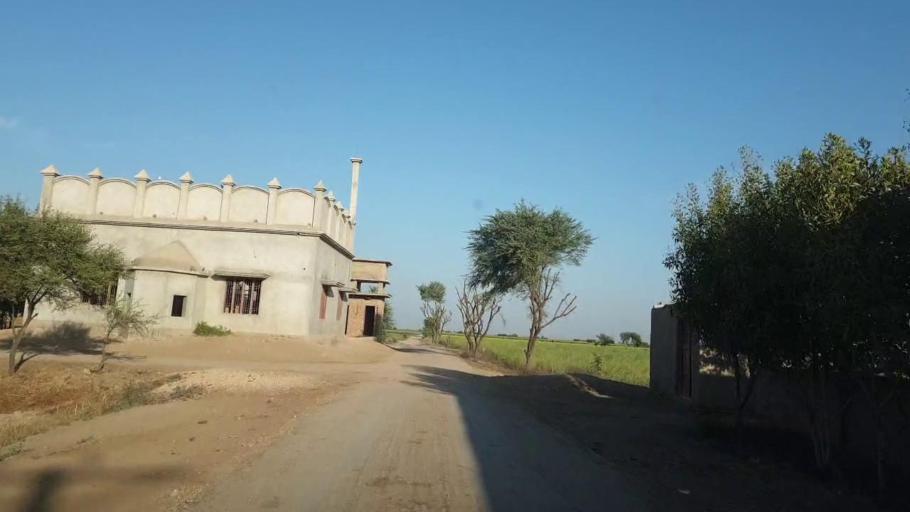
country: PK
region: Sindh
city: Kunri
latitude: 25.0910
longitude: 69.4429
